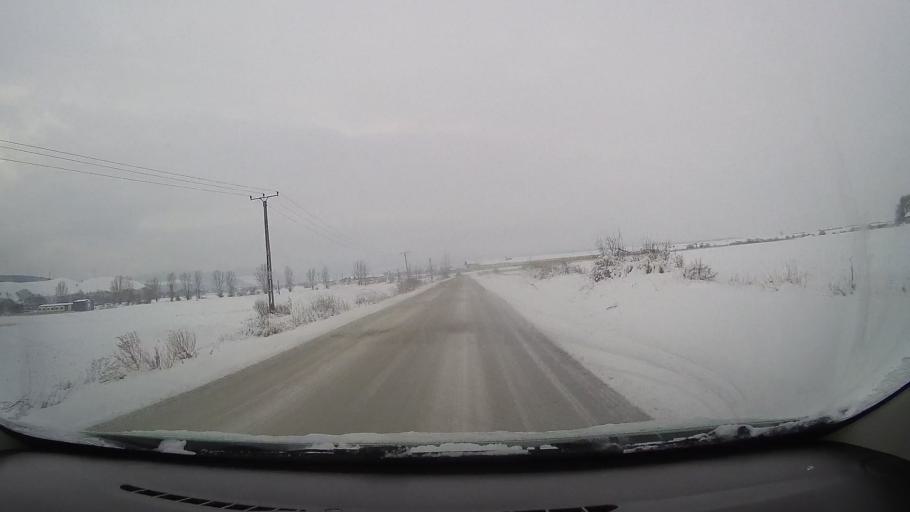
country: RO
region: Alba
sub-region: Comuna Pianu
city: Pianu de Jos
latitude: 45.9633
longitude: 23.4772
